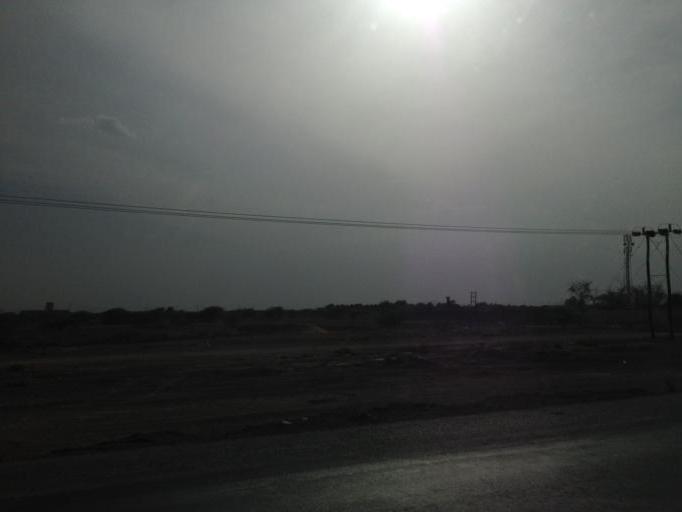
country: OM
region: Ash Sharqiyah
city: Al Qabil
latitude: 22.6108
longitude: 58.6642
